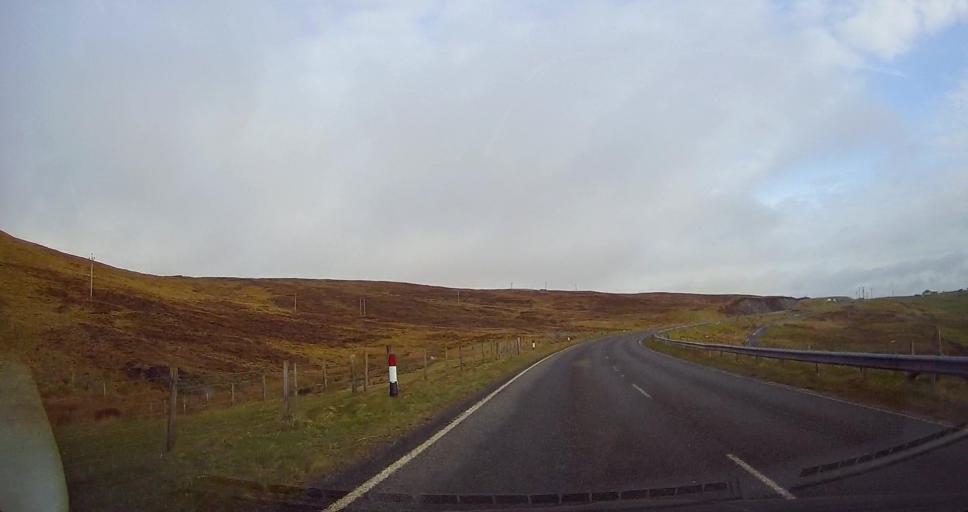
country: GB
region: Scotland
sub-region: Shetland Islands
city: Sandwick
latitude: 60.0710
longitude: -1.2298
